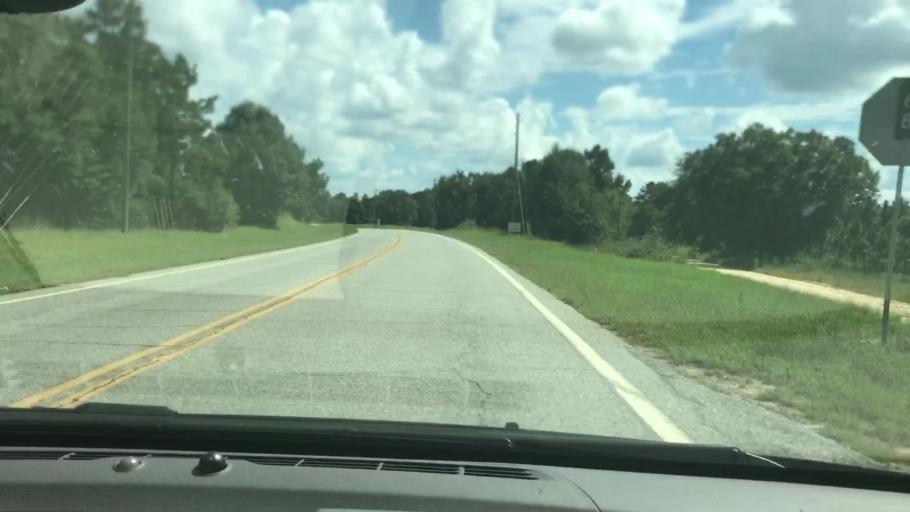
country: US
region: Georgia
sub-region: Clay County
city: Fort Gaines
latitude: 31.6531
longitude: -85.0473
